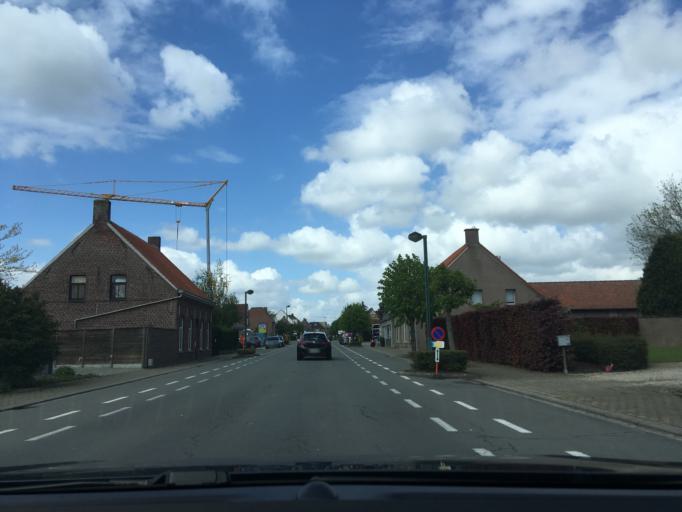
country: BE
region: Flanders
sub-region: Provincie West-Vlaanderen
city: Pittem
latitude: 50.9927
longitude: 3.2764
